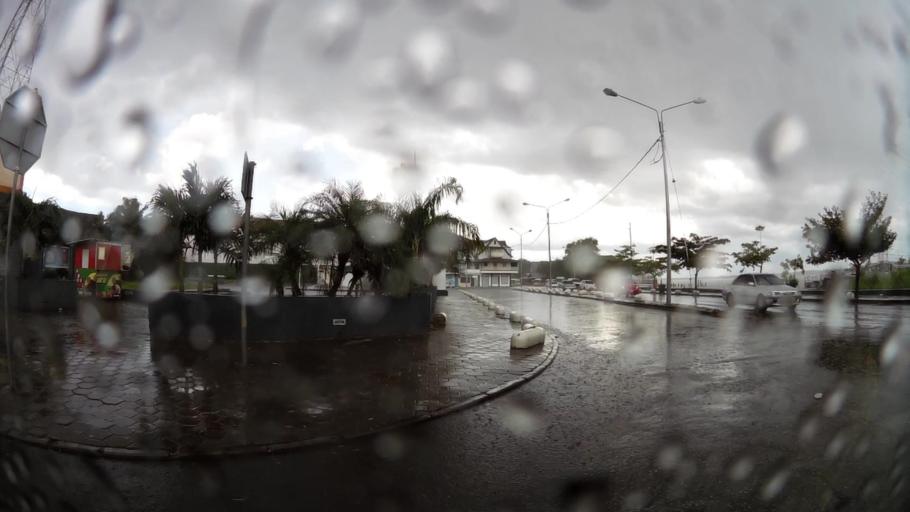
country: SR
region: Paramaribo
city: Paramaribo
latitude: 5.8244
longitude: -55.1565
